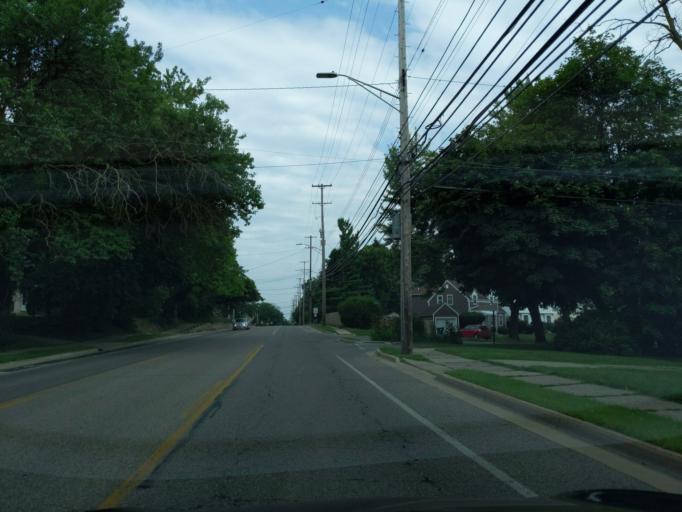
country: US
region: Michigan
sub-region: Ingham County
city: East Lansing
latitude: 42.7406
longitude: -84.4762
